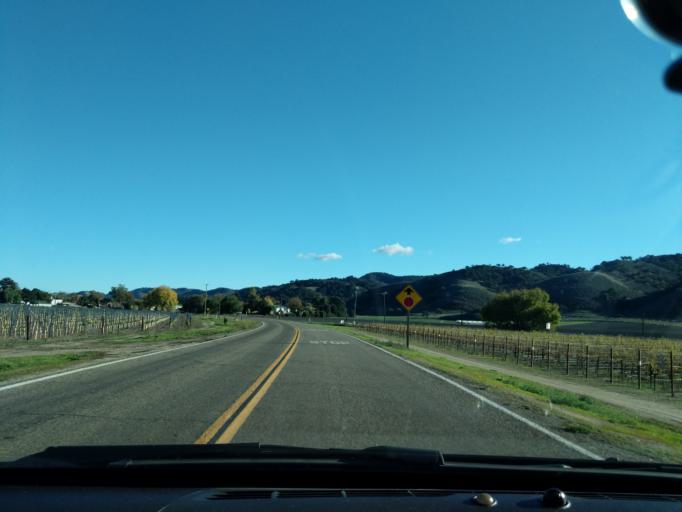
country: US
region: California
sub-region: Santa Barbara County
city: Los Alamos
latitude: 34.7467
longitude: -120.2886
